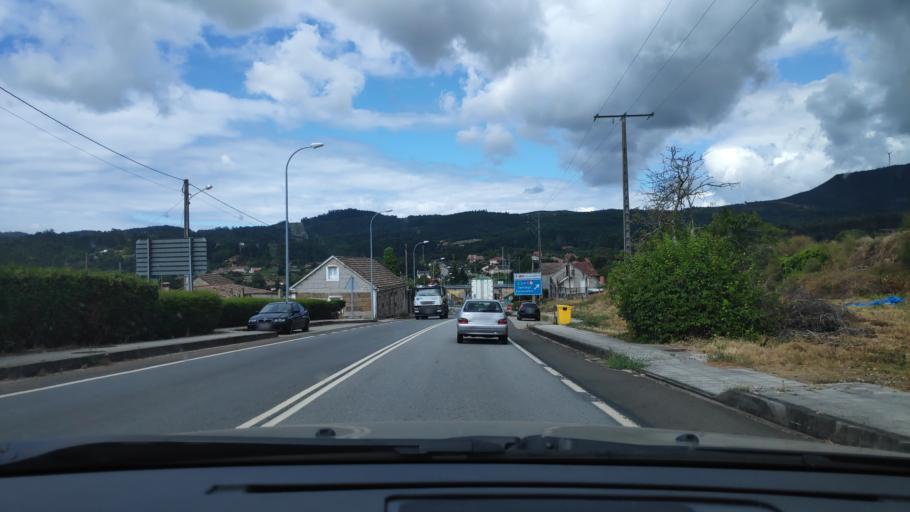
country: ES
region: Galicia
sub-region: Provincia de Pontevedra
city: Portas
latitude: 42.5945
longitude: -8.6812
